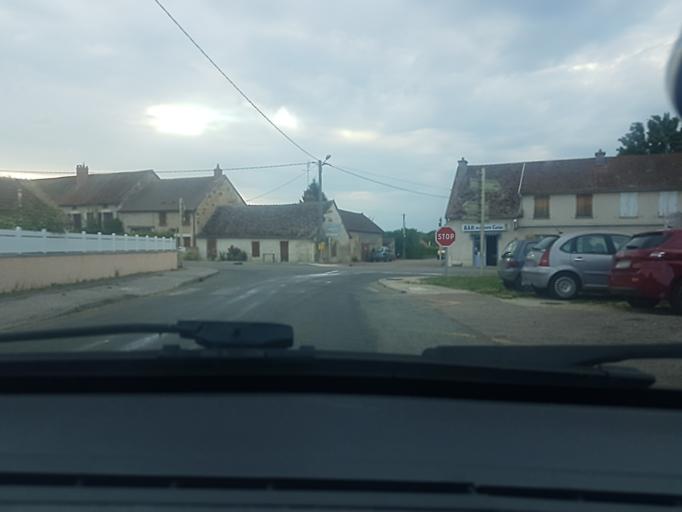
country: FR
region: Bourgogne
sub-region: Departement de Saone-et-Loire
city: Buxy
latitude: 46.7224
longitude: 4.7628
